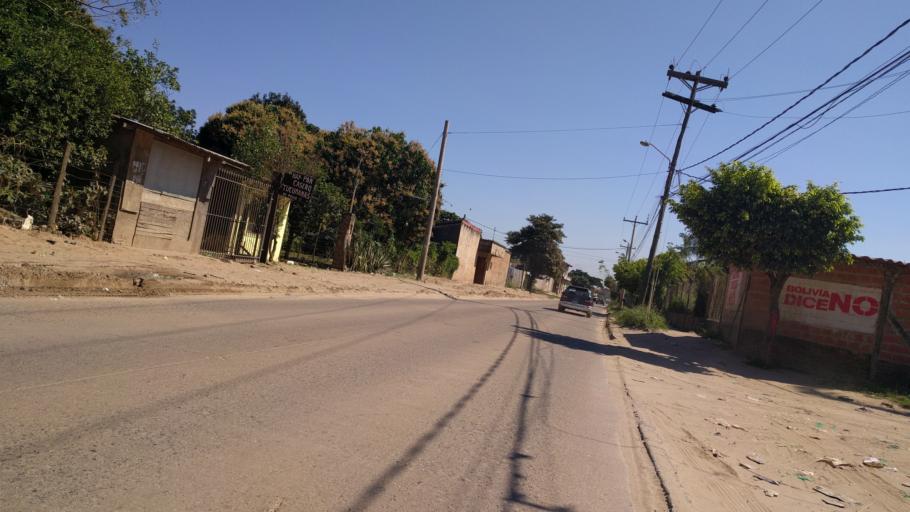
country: BO
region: Santa Cruz
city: Santa Cruz de la Sierra
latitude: -17.8403
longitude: -63.2187
